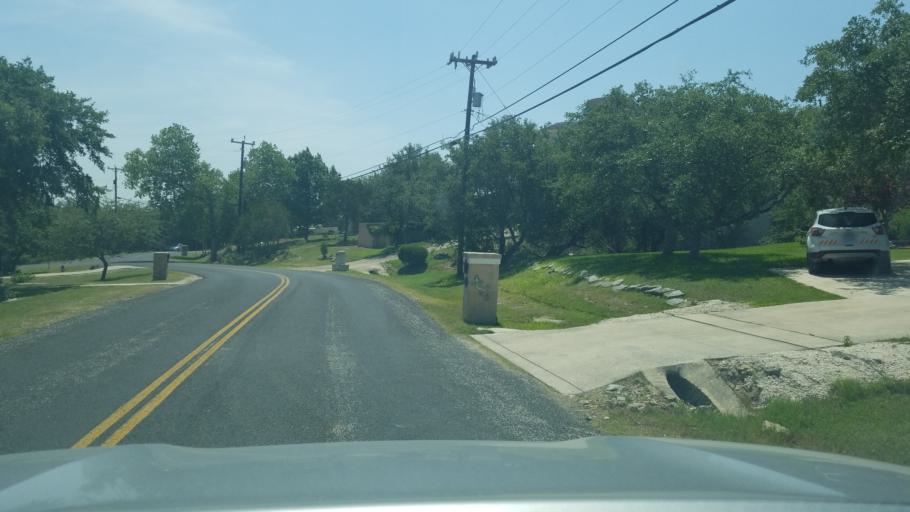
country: US
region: Texas
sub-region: Bexar County
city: Timberwood Park
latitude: 29.6942
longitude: -98.4832
